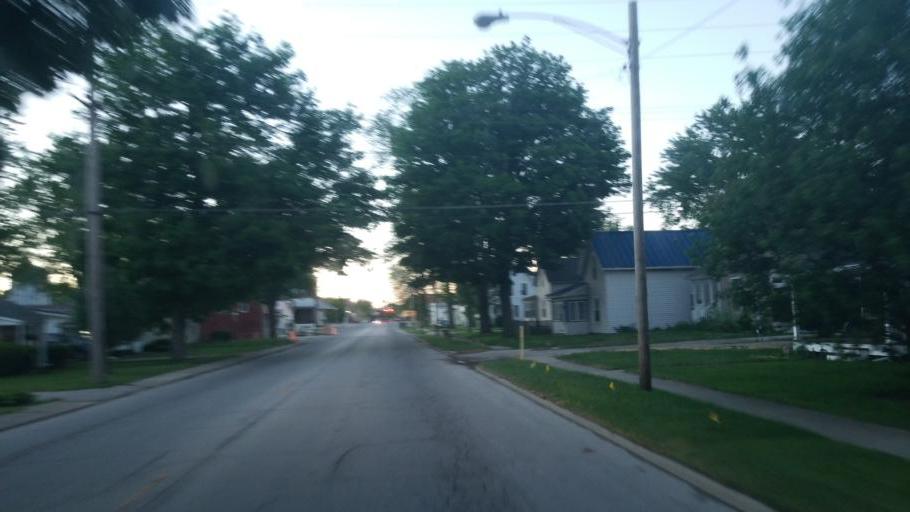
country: US
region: Indiana
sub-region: Elkhart County
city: Nappanee
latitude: 41.4390
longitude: -86.0013
